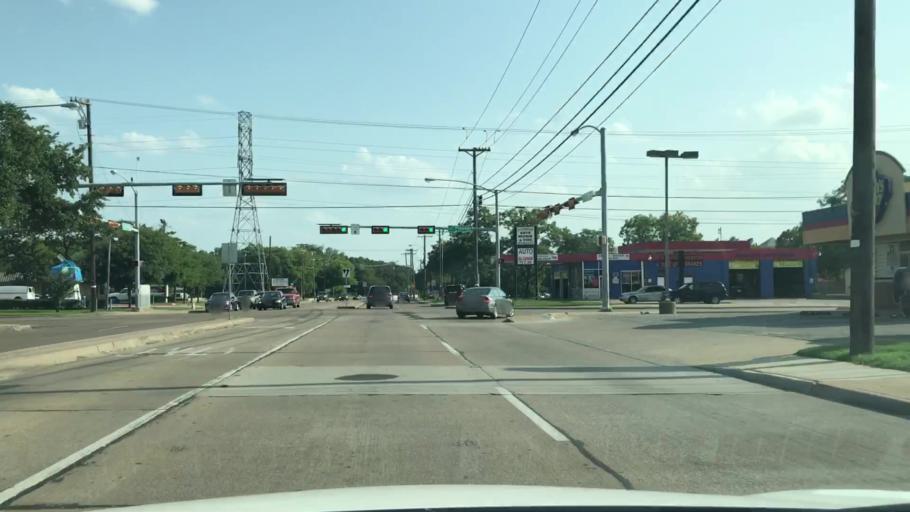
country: US
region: Texas
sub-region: Dallas County
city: Irving
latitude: 32.8185
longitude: -96.9495
